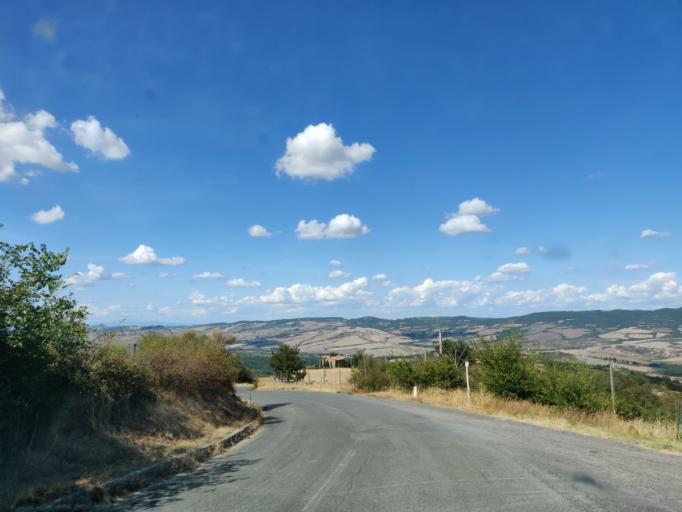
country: IT
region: Tuscany
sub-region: Provincia di Siena
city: Radicofani
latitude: 42.9652
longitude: 11.7319
